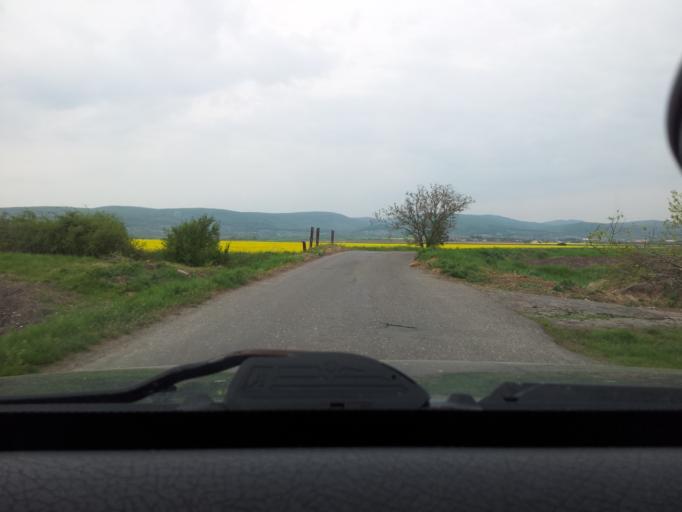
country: SK
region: Nitriansky
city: Tlmace
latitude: 48.2664
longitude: 18.5775
